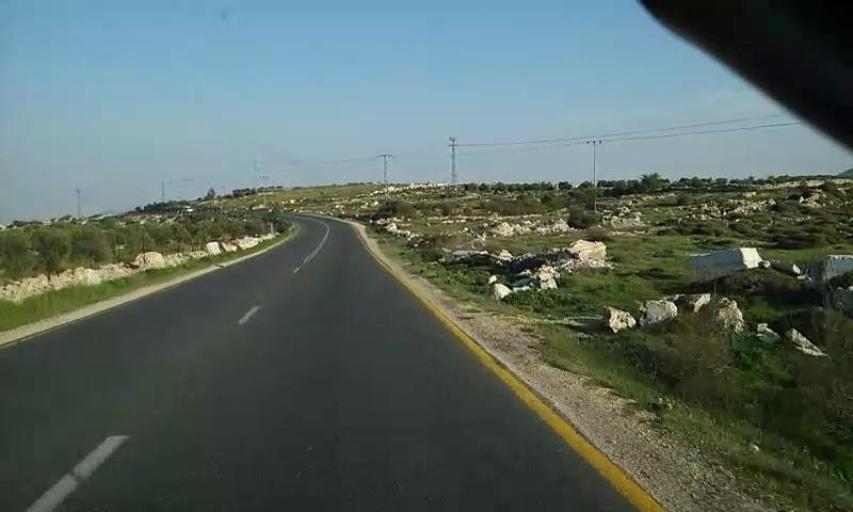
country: PS
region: West Bank
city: Marah Rabbah
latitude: 31.6470
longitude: 35.1873
